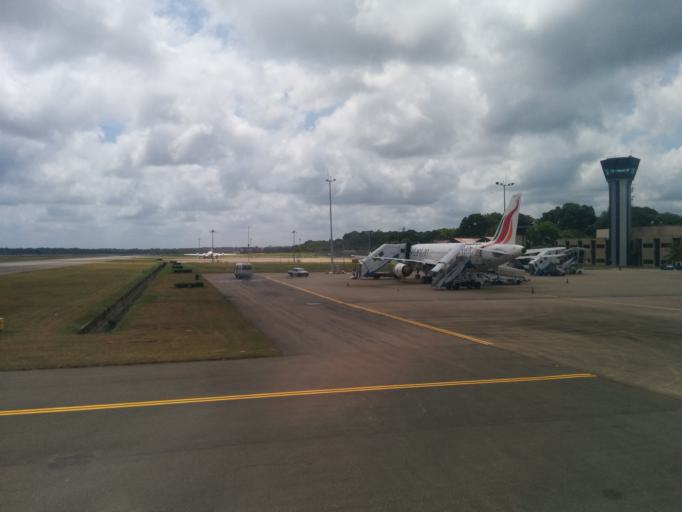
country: LK
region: Western
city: Katunayaka
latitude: 7.1785
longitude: 79.8846
